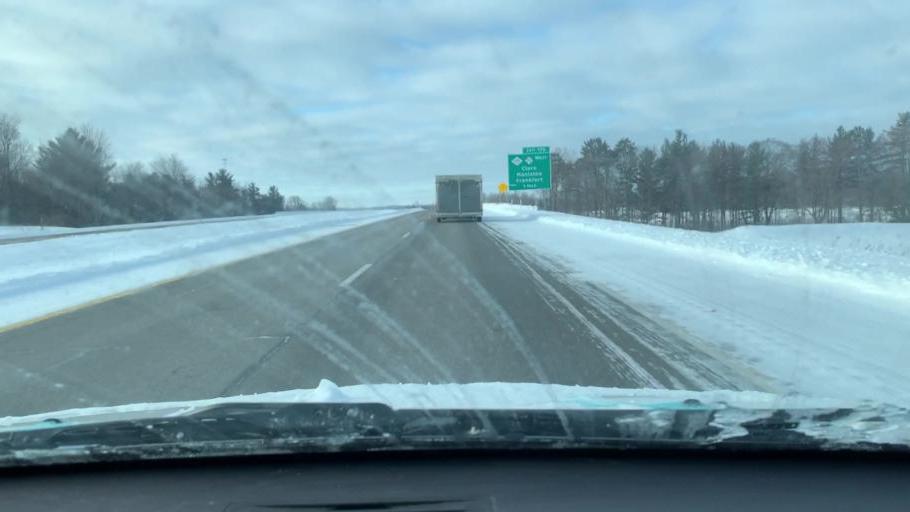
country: US
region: Michigan
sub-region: Wexford County
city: Cadillac
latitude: 44.2219
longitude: -85.3932
